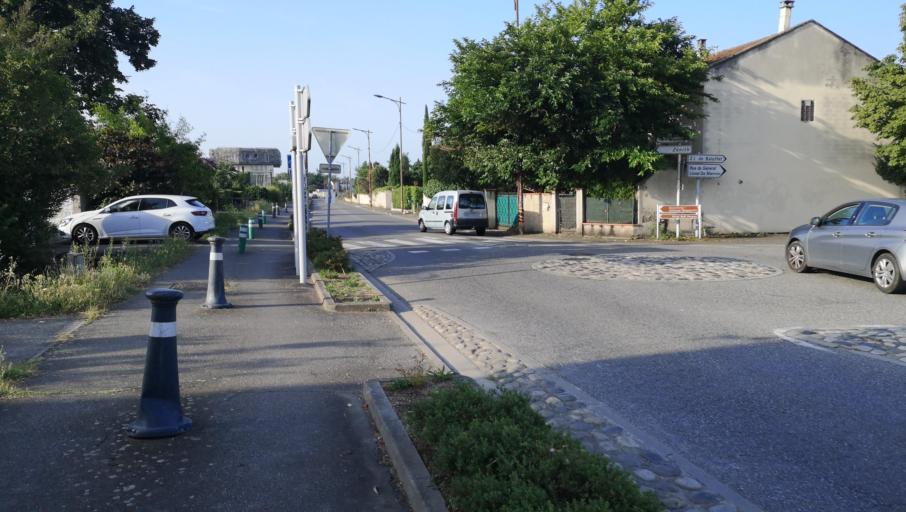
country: FR
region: Midi-Pyrenees
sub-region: Departement de la Haute-Garonne
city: Blagnac
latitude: 43.6015
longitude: 1.3933
